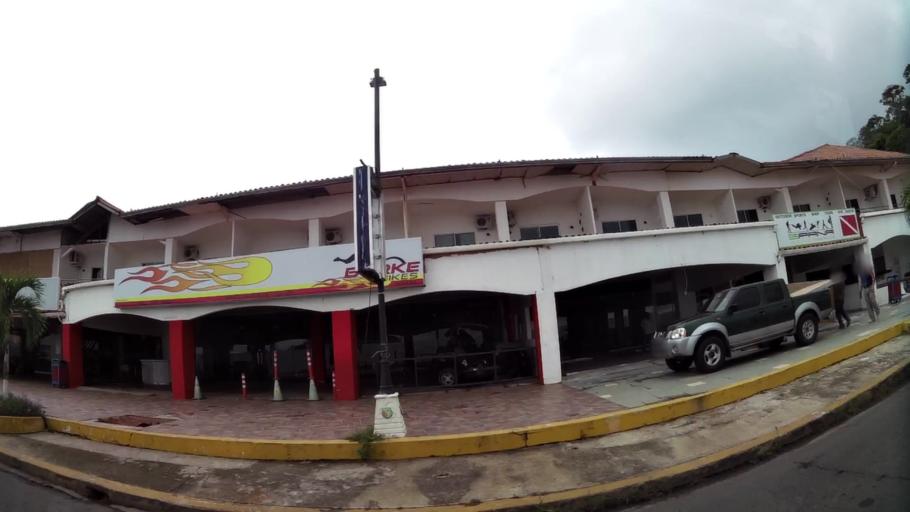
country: PA
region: Panama
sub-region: Distrito de Panama
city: Ancon
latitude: 8.9151
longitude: -79.5264
